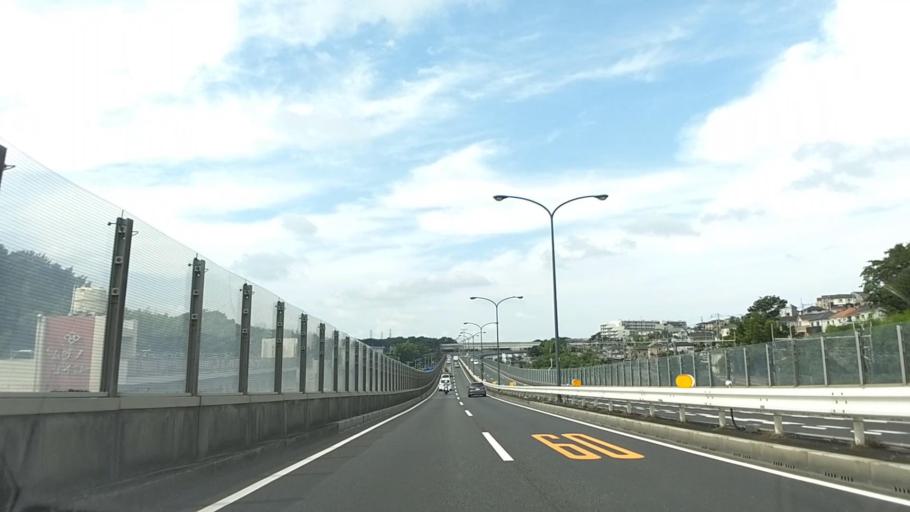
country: JP
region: Kanagawa
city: Yokohama
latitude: 35.4907
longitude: 139.5982
